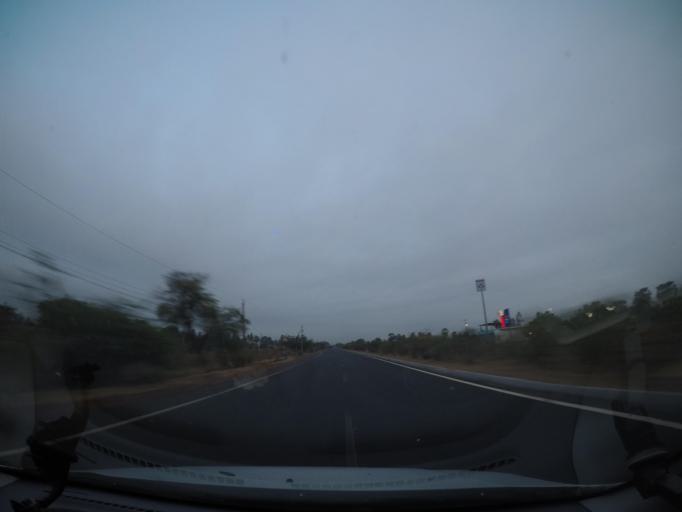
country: IN
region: Andhra Pradesh
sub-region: West Godavari
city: Tadepallegudem
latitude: 16.8100
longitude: 81.3327
